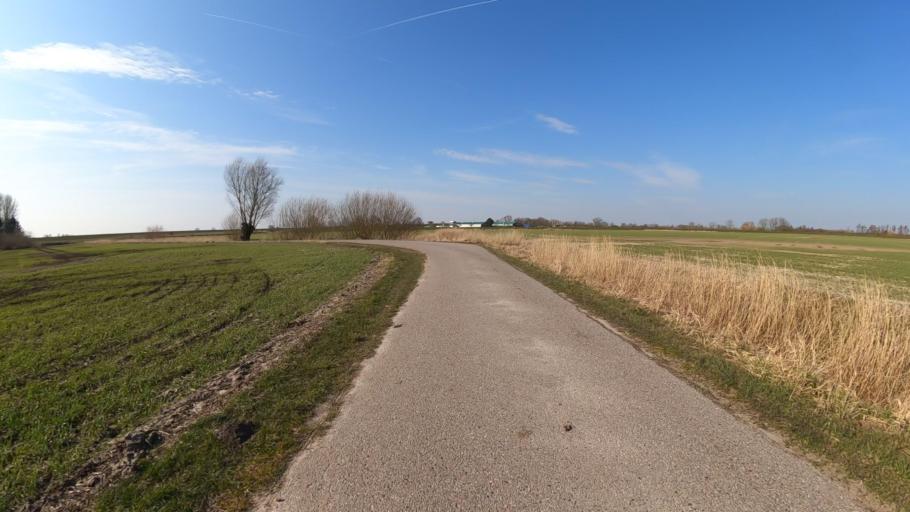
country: DE
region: Schleswig-Holstein
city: Seestermuhe
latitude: 53.7130
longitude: 9.5332
